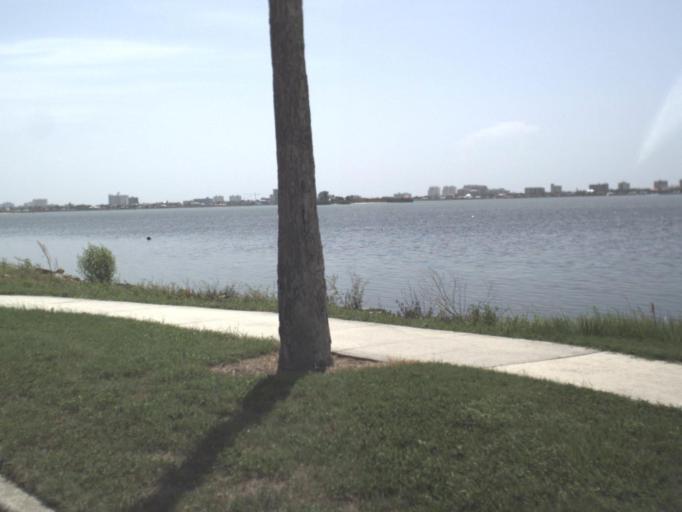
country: US
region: Florida
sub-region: Pinellas County
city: Dunedin
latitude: 27.9985
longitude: -82.7941
